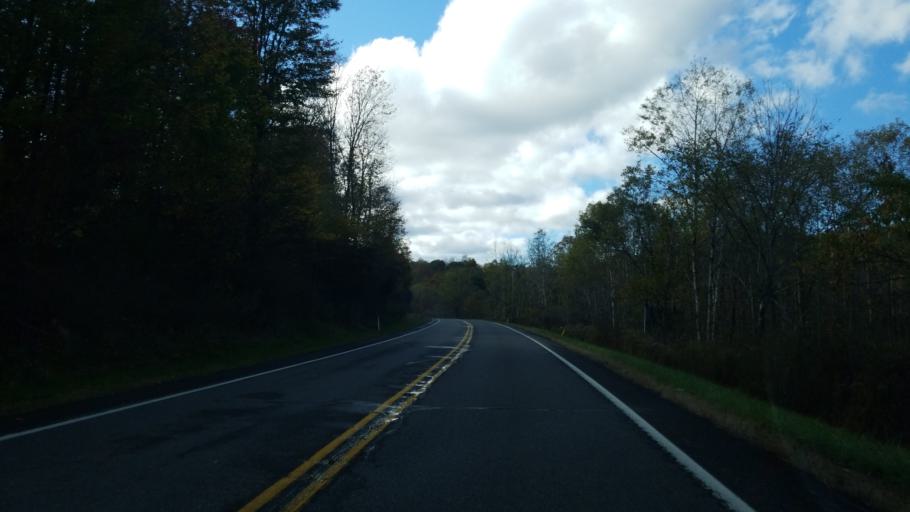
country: US
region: Pennsylvania
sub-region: Jefferson County
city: Sykesville
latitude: 41.0920
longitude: -78.8224
